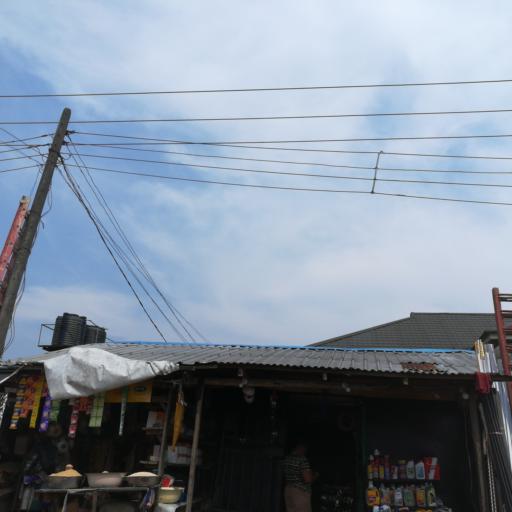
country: NG
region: Rivers
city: Port Harcourt
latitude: 4.8669
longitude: 7.0217
